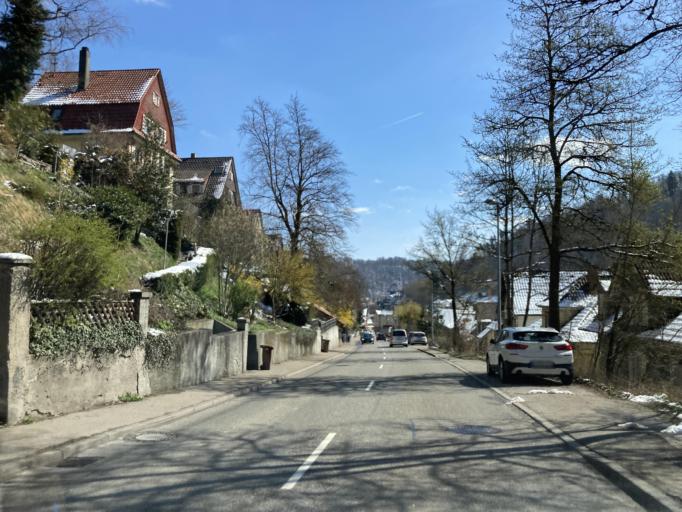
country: DE
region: Baden-Wuerttemberg
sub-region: Freiburg Region
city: Oberndorf
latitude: 48.2896
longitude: 8.5625
